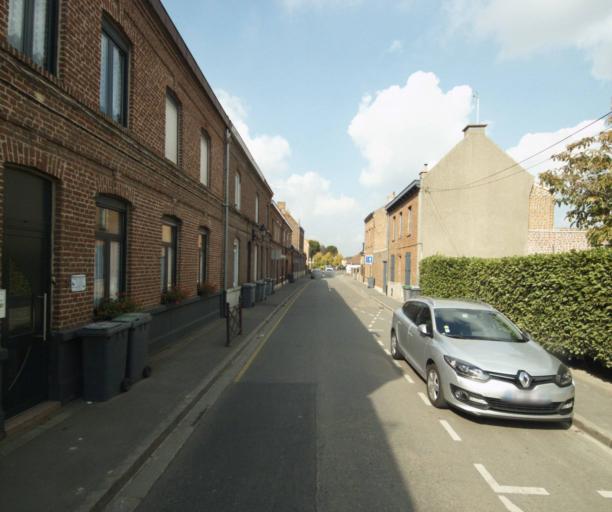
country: FR
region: Nord-Pas-de-Calais
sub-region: Departement du Nord
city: Houplin-Ancoisne
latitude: 50.5765
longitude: 3.0176
